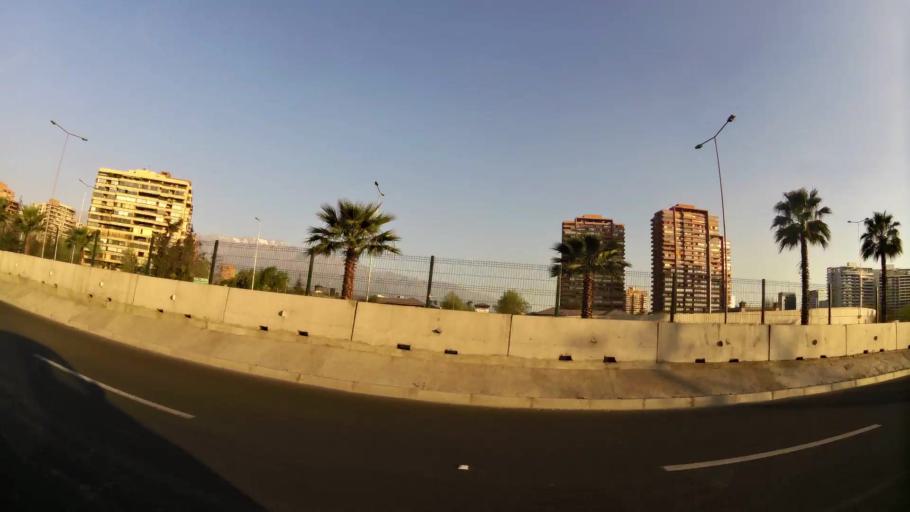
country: CL
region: Santiago Metropolitan
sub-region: Provincia de Santiago
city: Villa Presidente Frei, Nunoa, Santiago, Chile
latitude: -33.3971
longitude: -70.5697
